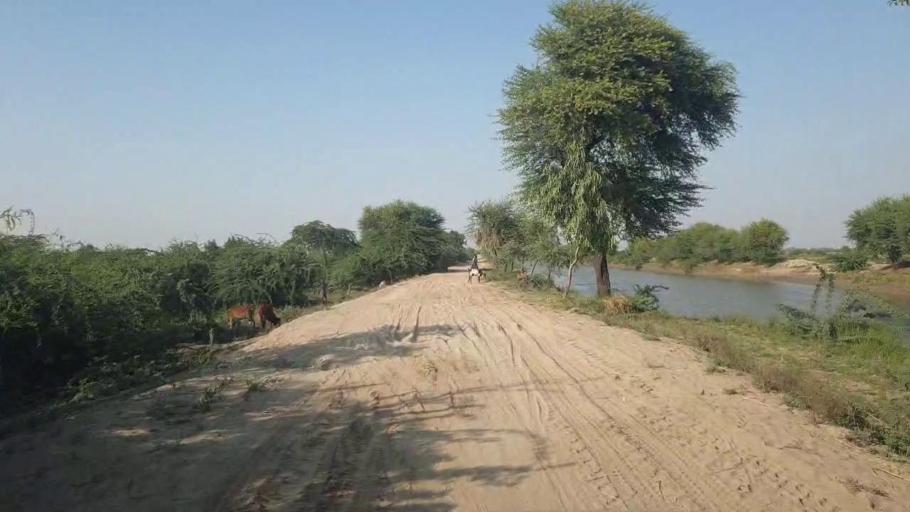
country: PK
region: Sindh
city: Badin
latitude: 24.6327
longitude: 68.8150
